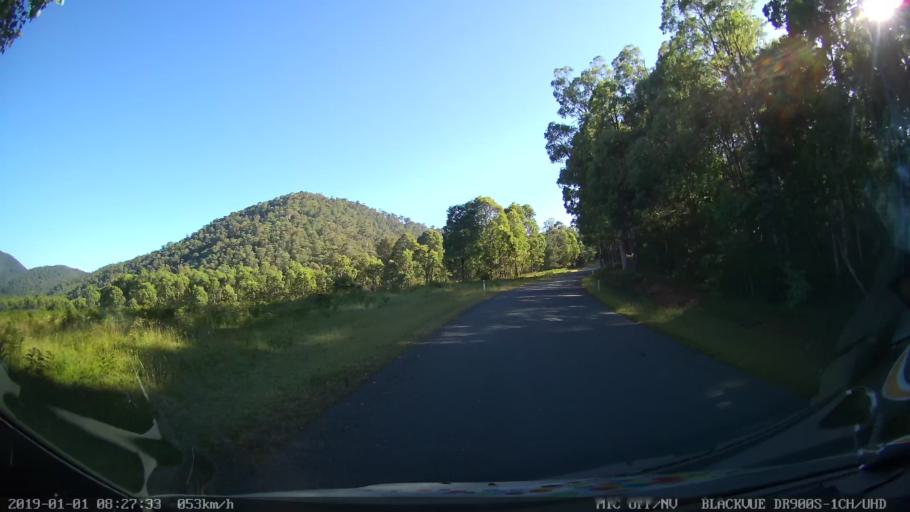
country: AU
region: New South Wales
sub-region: Snowy River
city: Jindabyne
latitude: -36.3807
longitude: 148.1843
